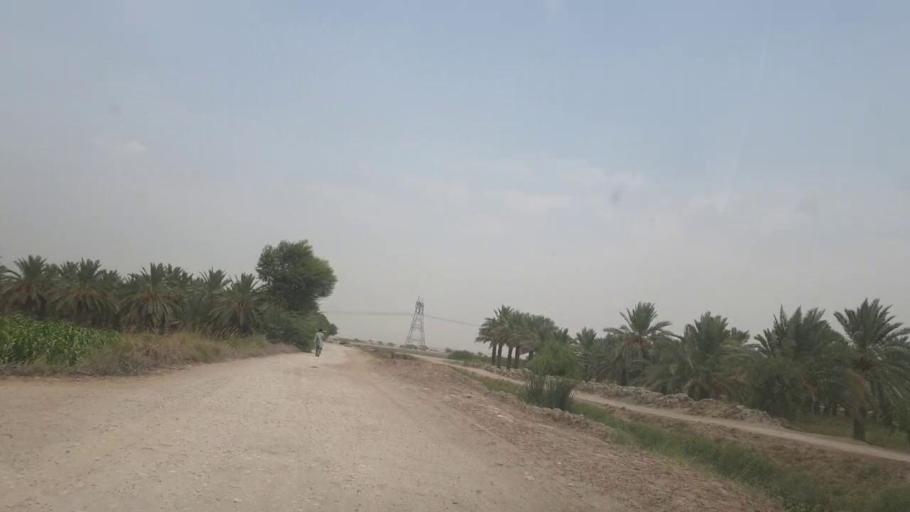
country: PK
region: Sindh
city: Kot Diji
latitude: 27.4250
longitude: 68.6815
